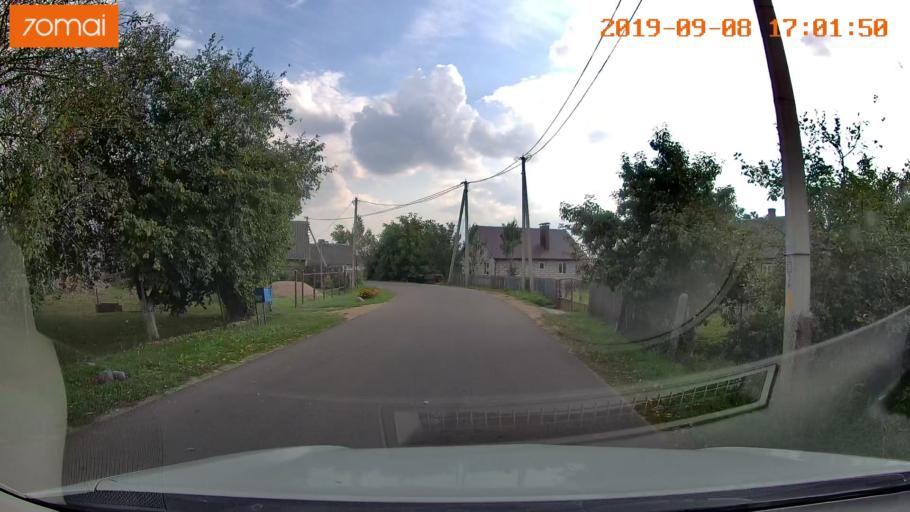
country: BY
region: Grodnenskaya
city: Hrodna
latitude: 53.7072
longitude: 23.9365
